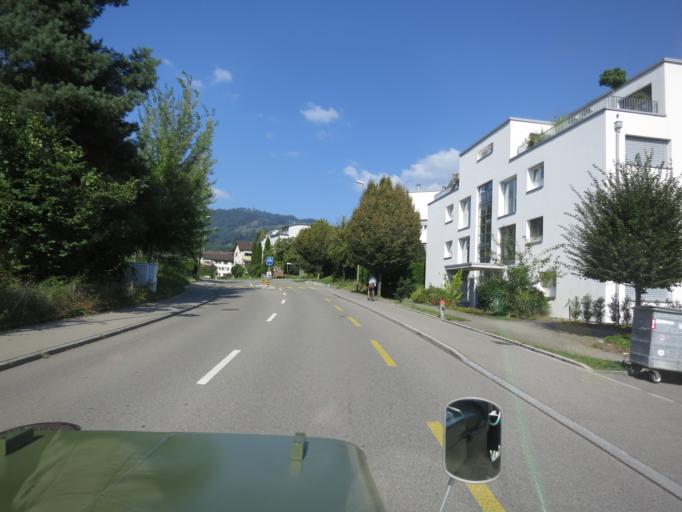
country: CH
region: Zurich
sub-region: Bezirk Hinwil
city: Rueti / Oberdorf
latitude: 47.2633
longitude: 8.8662
